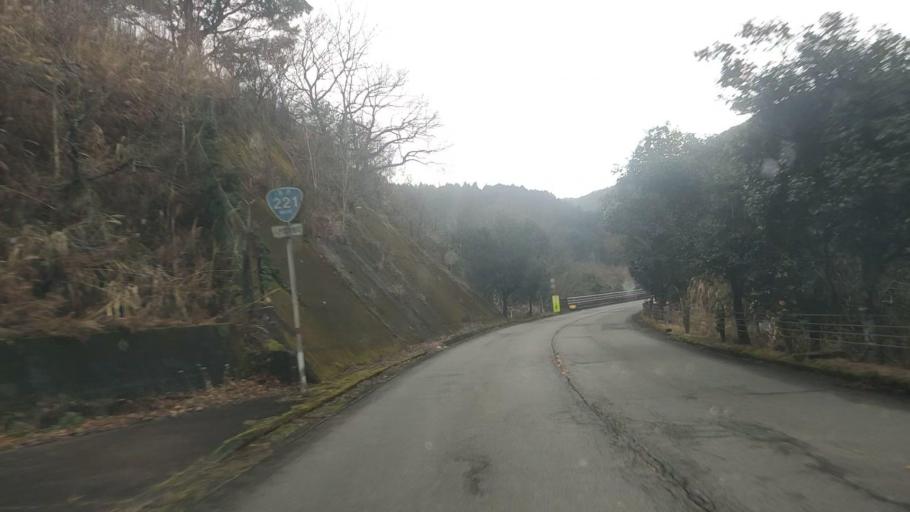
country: JP
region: Kumamoto
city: Hitoyoshi
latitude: 32.1244
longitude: 130.8124
